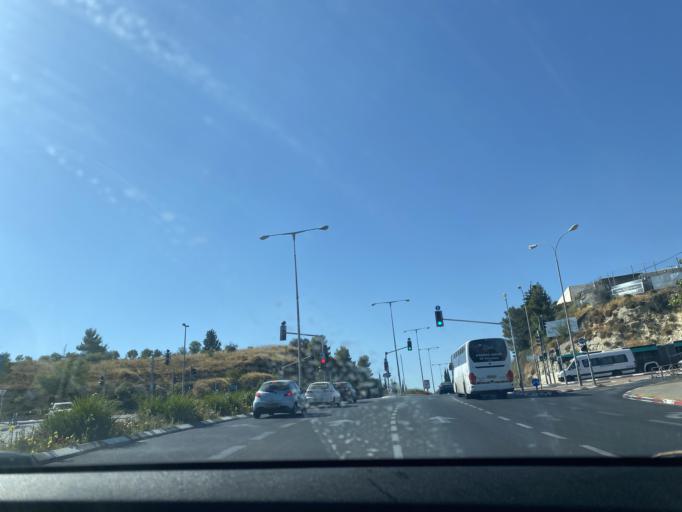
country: PS
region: West Bank
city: Bayt Iksa
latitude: 31.8212
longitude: 35.1897
